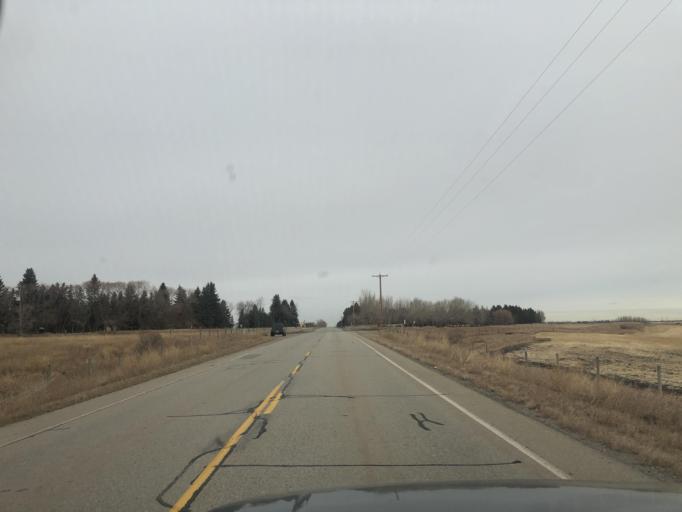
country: CA
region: Alberta
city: Chestermere
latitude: 50.9877
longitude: -113.8654
